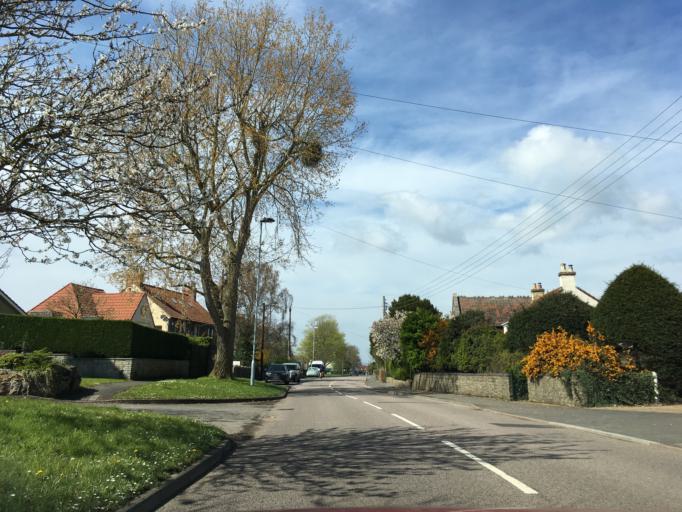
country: GB
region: England
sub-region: South Gloucestershire
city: Severn Beach
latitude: 51.5398
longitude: -2.6189
